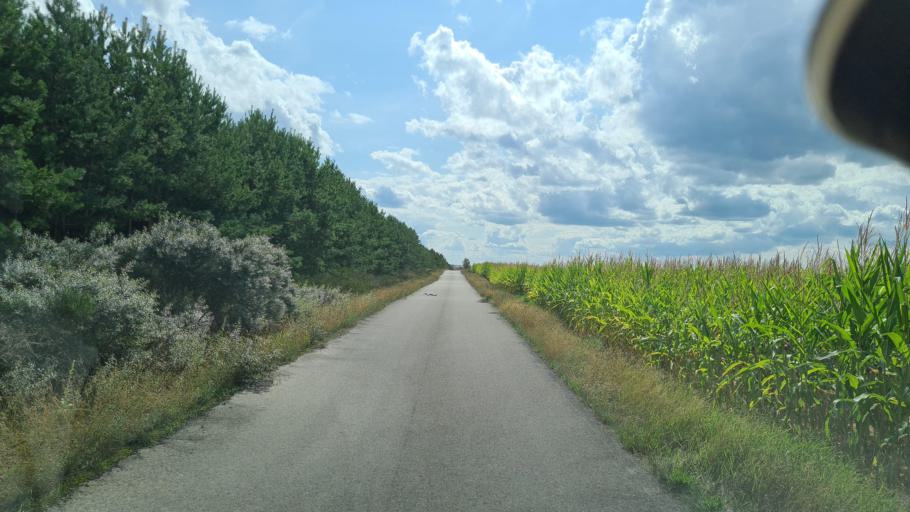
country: DE
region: Brandenburg
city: Drebkau
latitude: 51.6011
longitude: 14.2894
